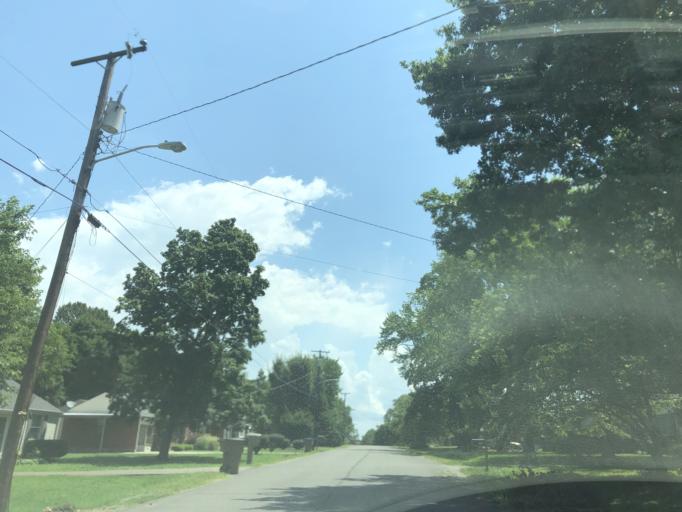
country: US
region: Tennessee
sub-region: Davidson County
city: Lakewood
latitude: 36.1575
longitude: -86.6583
